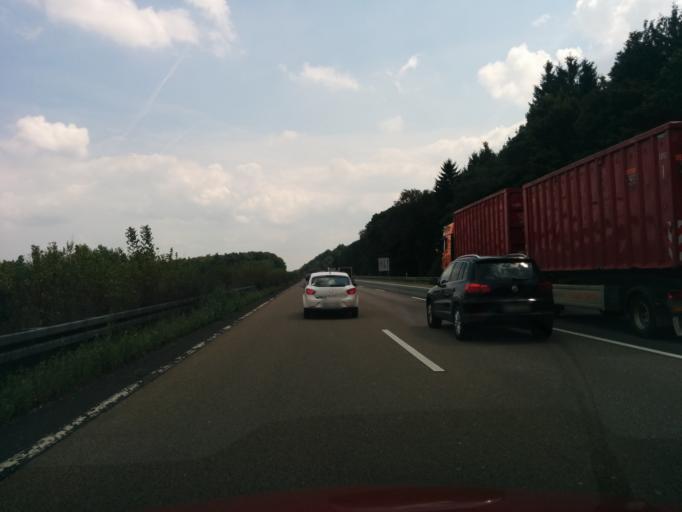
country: DE
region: Rheinland-Pfalz
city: Gorgeshausen
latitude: 50.4126
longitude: 7.9666
